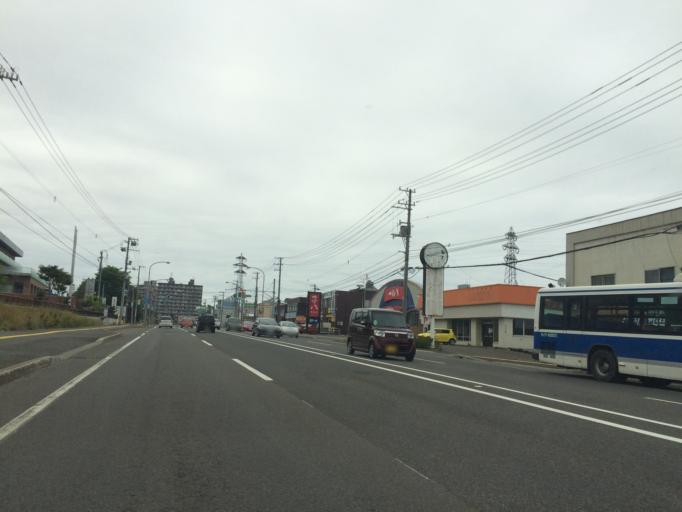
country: JP
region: Hokkaido
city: Sapporo
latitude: 43.1285
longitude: 141.2133
